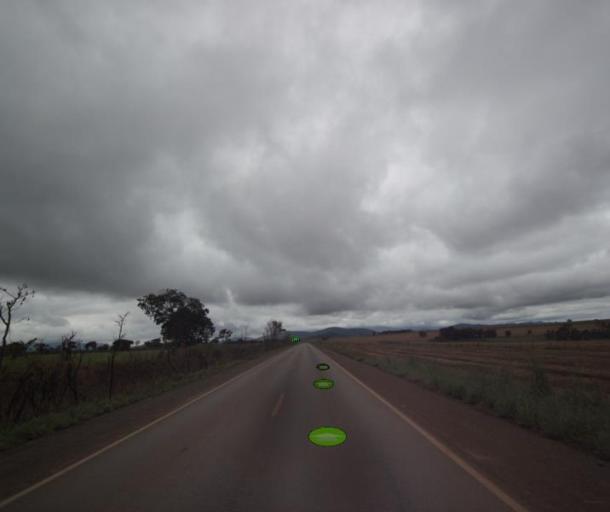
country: BR
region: Goias
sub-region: Barro Alto
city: Barro Alto
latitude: -14.8515
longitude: -49.0250
